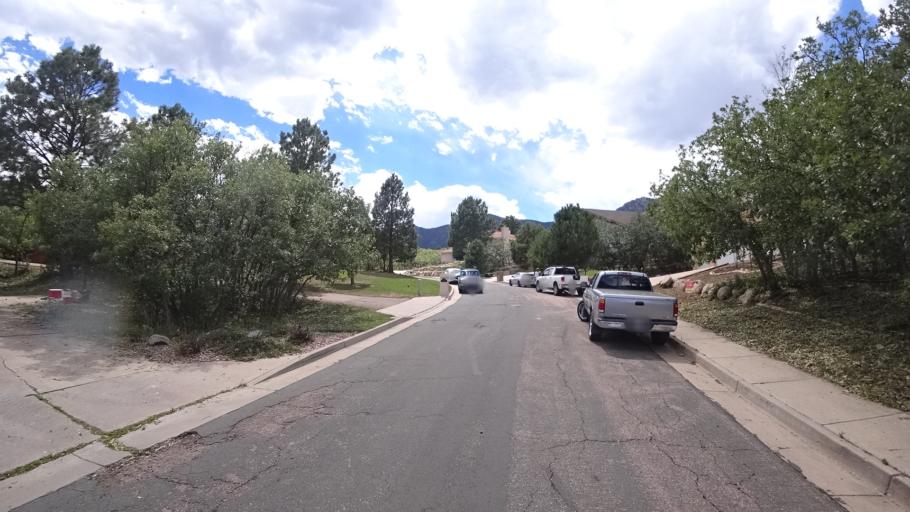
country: US
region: Colorado
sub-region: El Paso County
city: Stratmoor
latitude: 38.7693
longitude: -104.8313
